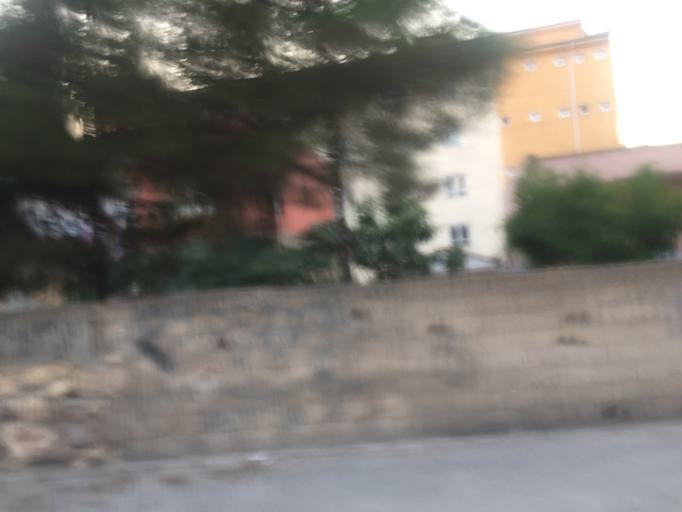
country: TR
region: Mardin
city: Midyat
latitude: 37.4301
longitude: 41.3385
